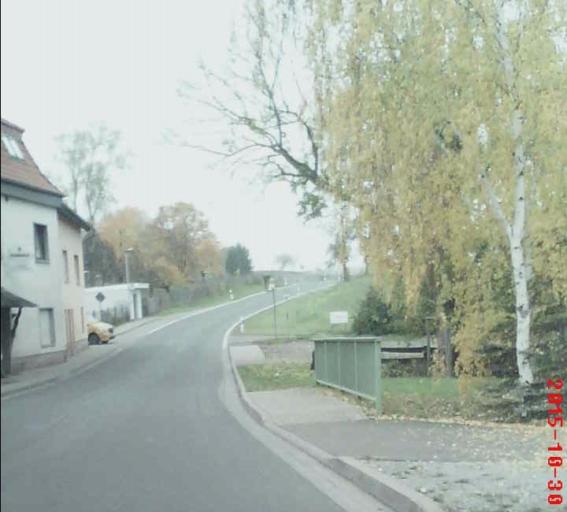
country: DE
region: Thuringia
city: Anrode
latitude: 51.2396
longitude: 10.3746
